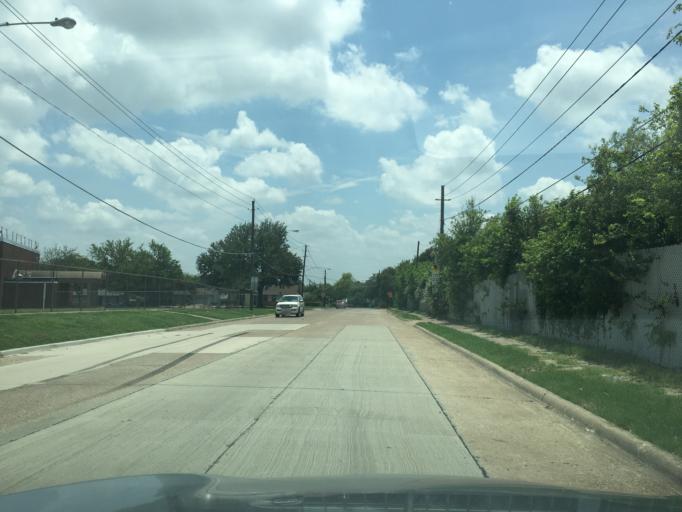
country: US
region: Texas
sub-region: Dallas County
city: Richardson
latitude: 32.9178
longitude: -96.7615
